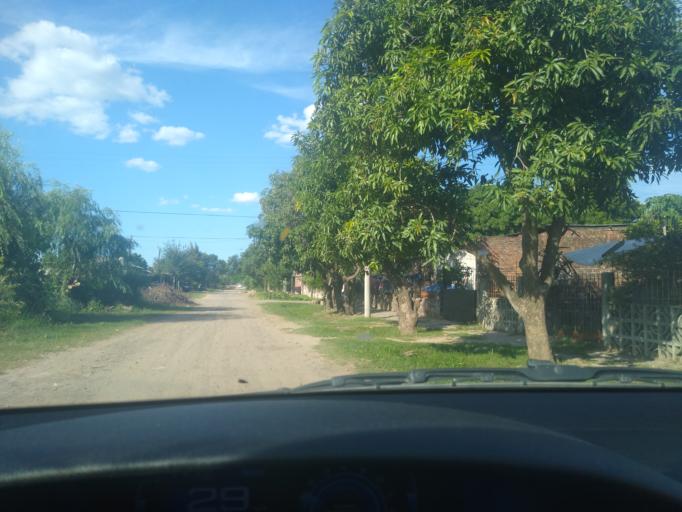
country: AR
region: Chaco
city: Barranqueras
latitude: -27.4807
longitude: -58.9301
